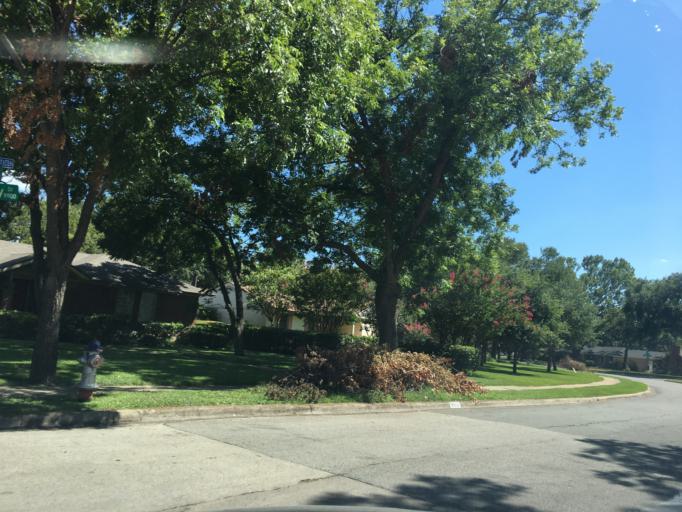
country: US
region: Texas
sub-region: Dallas County
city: Garland
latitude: 32.8400
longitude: -96.6981
